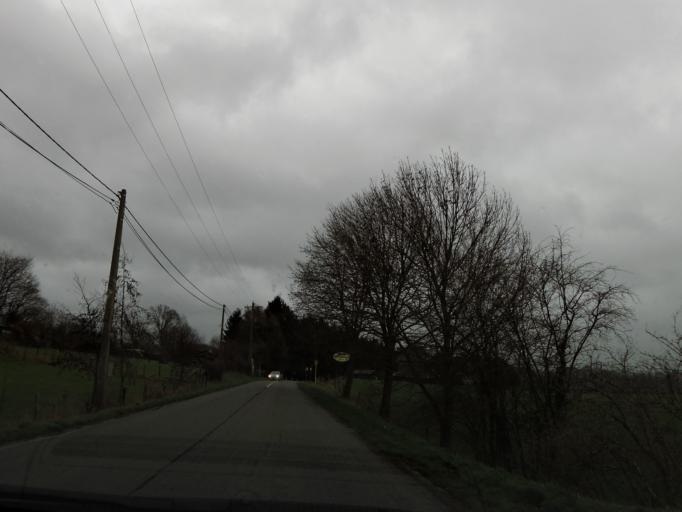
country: BE
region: Wallonia
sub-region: Province de Liege
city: Plombieres
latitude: 50.7524
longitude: 5.9725
